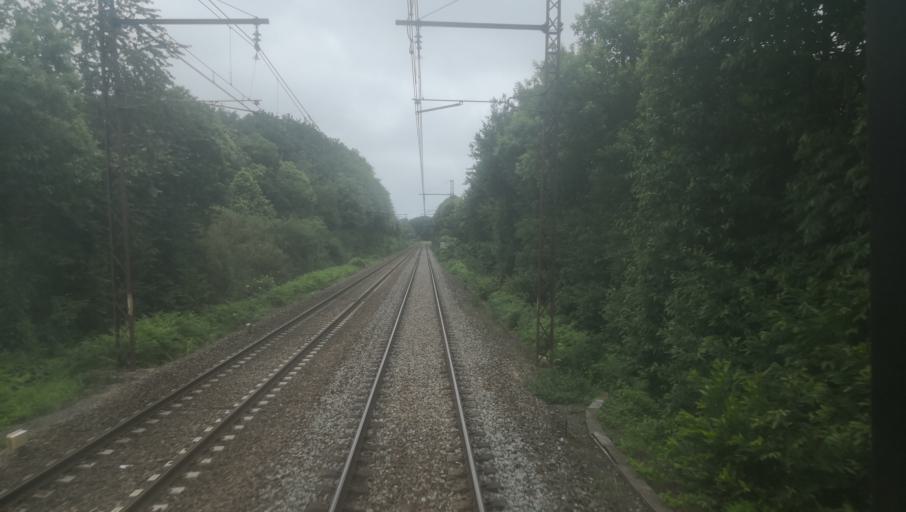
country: FR
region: Limousin
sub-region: Departement de la Creuse
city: La Souterraine
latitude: 46.2675
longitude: 1.4741
